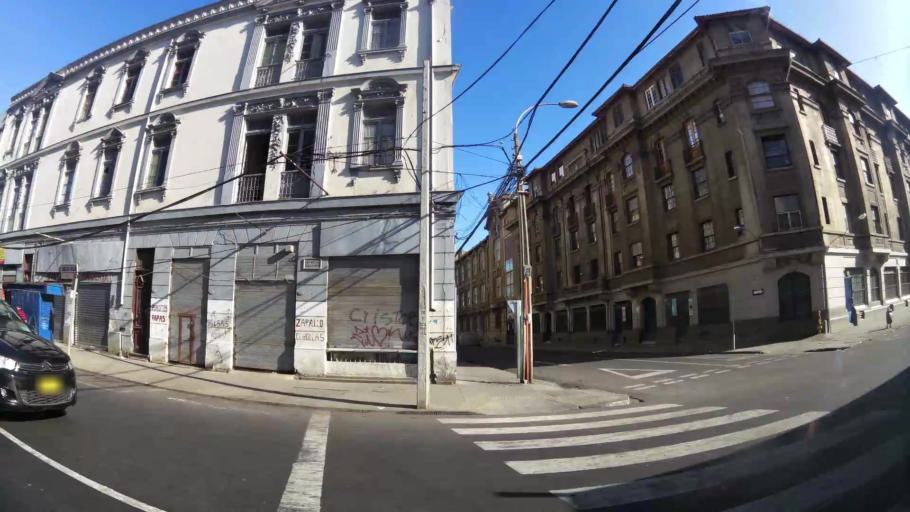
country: CL
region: Valparaiso
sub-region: Provincia de Valparaiso
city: Valparaiso
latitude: -33.0454
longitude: -71.6061
